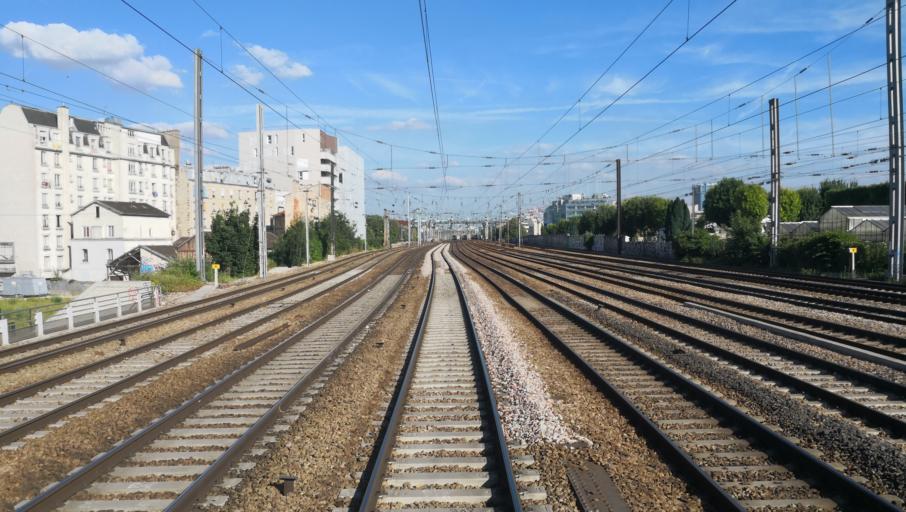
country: FR
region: Ile-de-France
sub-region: Departement des Hauts-de-Seine
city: Levallois-Perret
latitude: 48.9030
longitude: 2.2886
